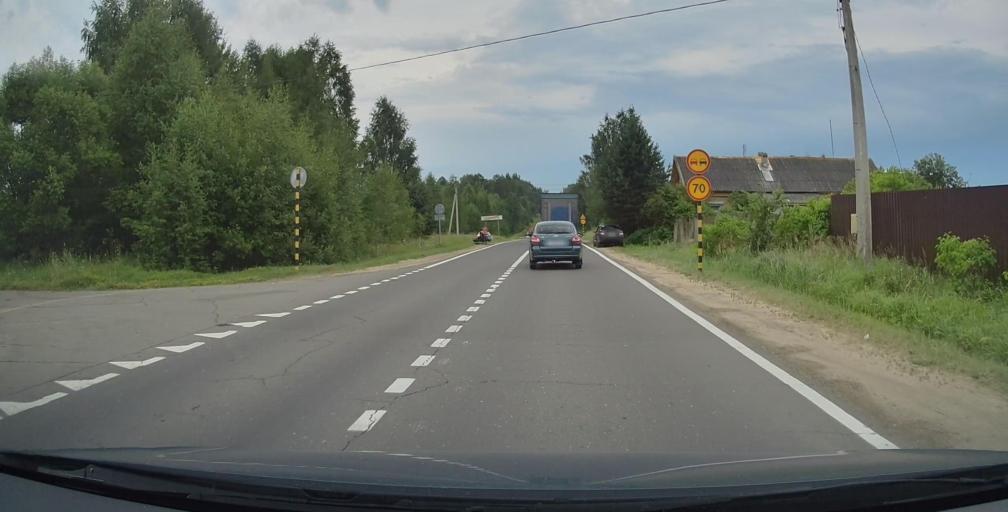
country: RU
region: Jaroslavl
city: Myshkin
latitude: 57.8571
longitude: 38.5092
